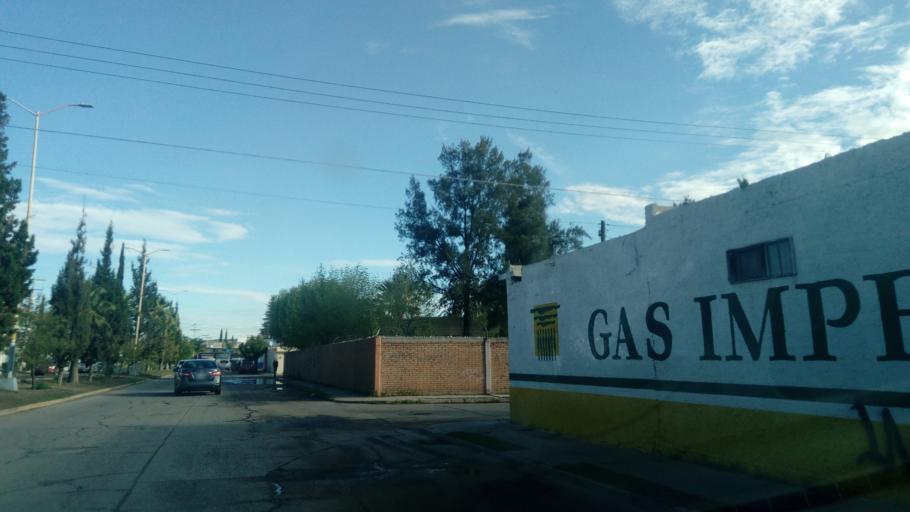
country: MX
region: Durango
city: Victoria de Durango
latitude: 24.0543
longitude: -104.6087
